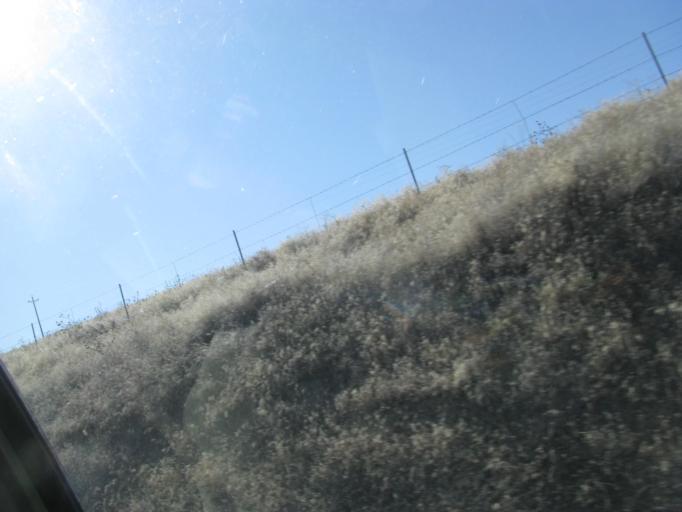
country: US
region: Washington
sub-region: Asotin County
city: Asotin
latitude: 46.3267
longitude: -117.0589
